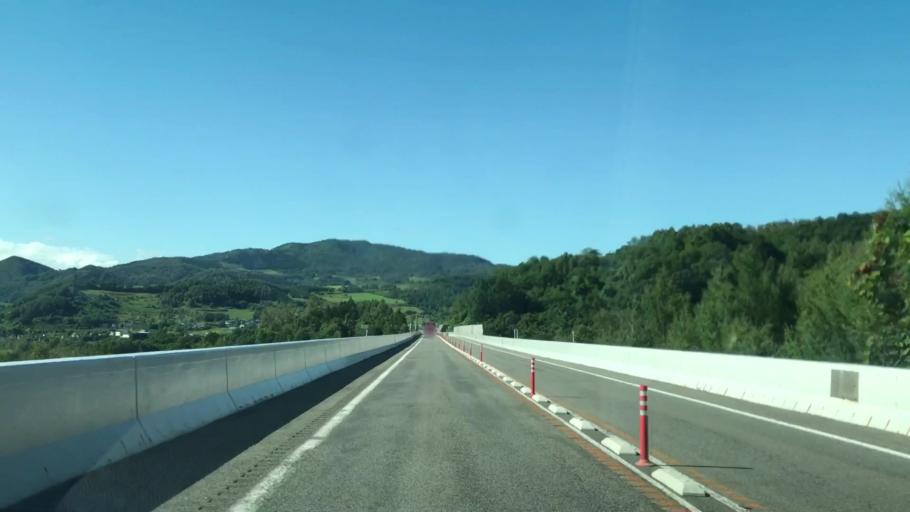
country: JP
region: Hokkaido
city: Date
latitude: 42.5371
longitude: 140.7970
